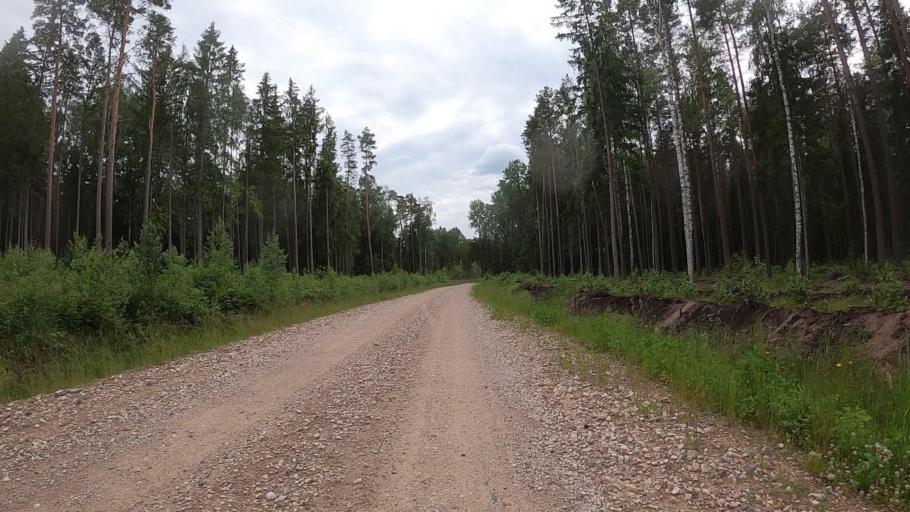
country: LV
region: Olaine
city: Olaine
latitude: 56.7608
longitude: 23.8805
